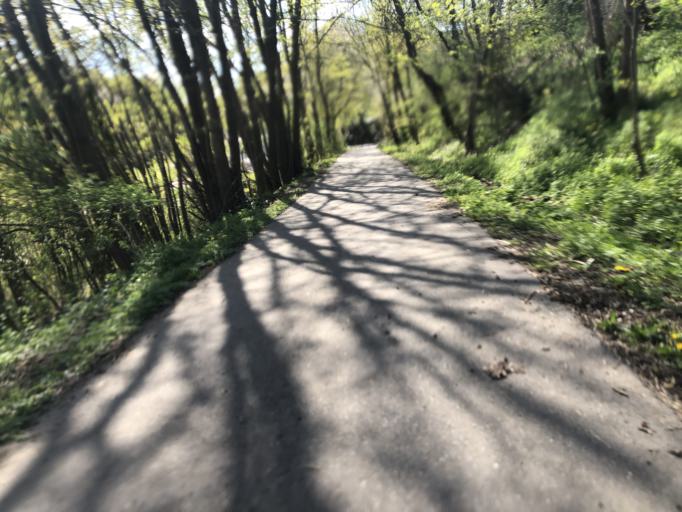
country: DE
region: North Rhine-Westphalia
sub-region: Regierungsbezirk Koln
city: Mechernich
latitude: 50.6311
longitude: 6.6271
